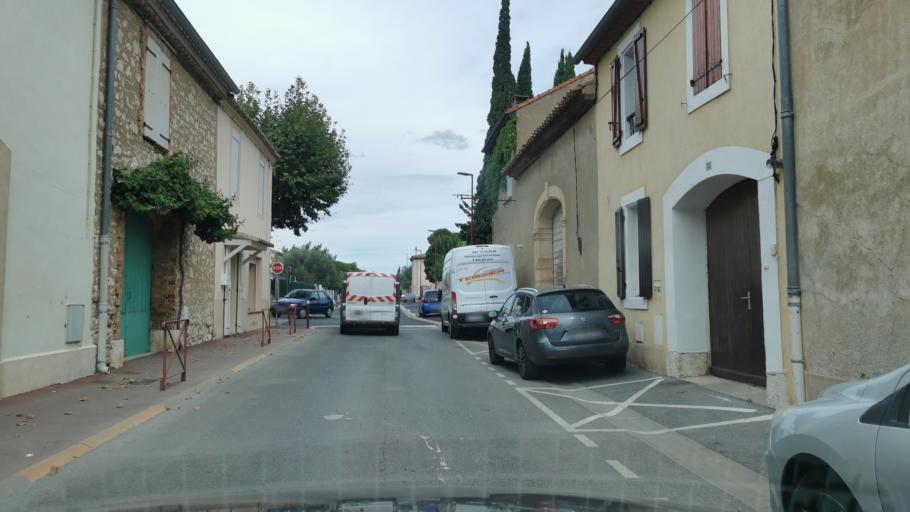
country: FR
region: Languedoc-Roussillon
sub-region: Departement de l'Aude
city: Saint-Marcel-sur-Aude
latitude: 43.2597
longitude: 2.9449
